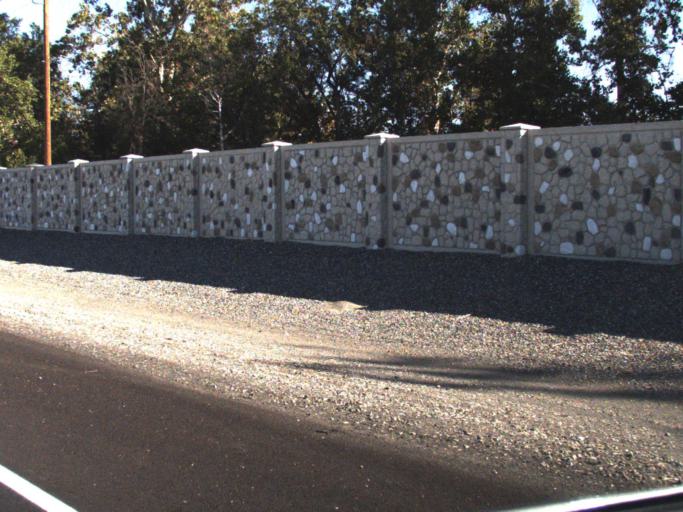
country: US
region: Washington
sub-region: Benton County
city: Richland
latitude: 46.2809
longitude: -119.3064
